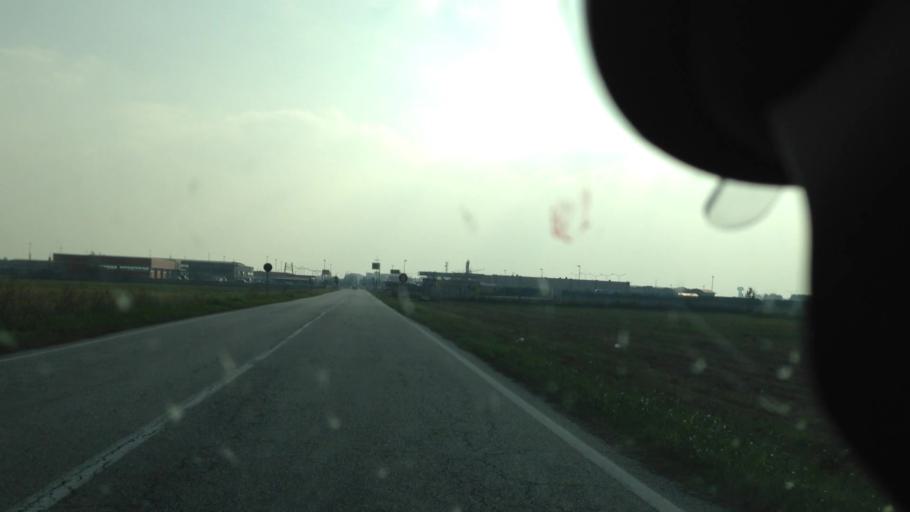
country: IT
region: Piedmont
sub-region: Provincia di Vercelli
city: Cigliano
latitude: 45.3224
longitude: 8.0331
